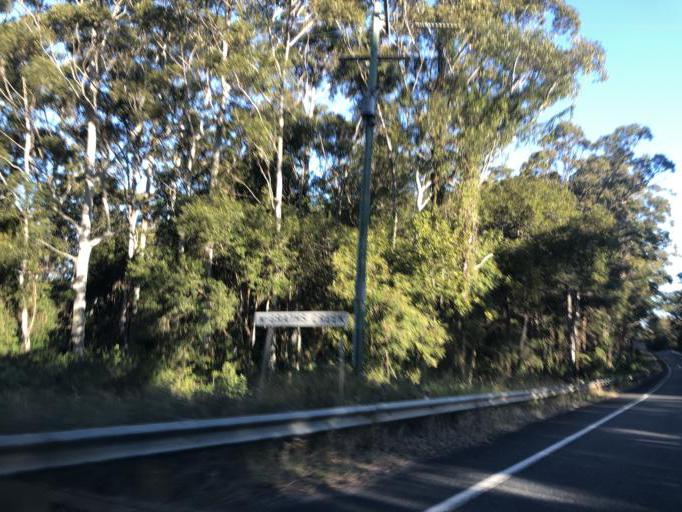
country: AU
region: New South Wales
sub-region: Nambucca Shire
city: Nambucca
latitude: -30.5516
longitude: 153.0083
